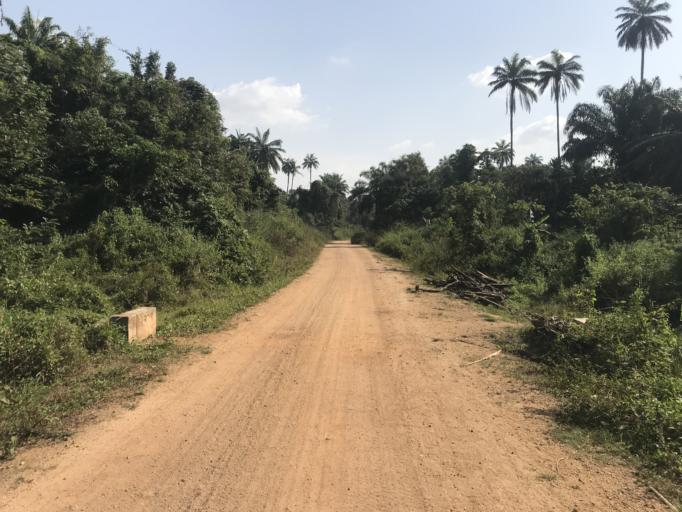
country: NG
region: Osun
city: Ikirun
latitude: 7.8814
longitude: 4.5862
